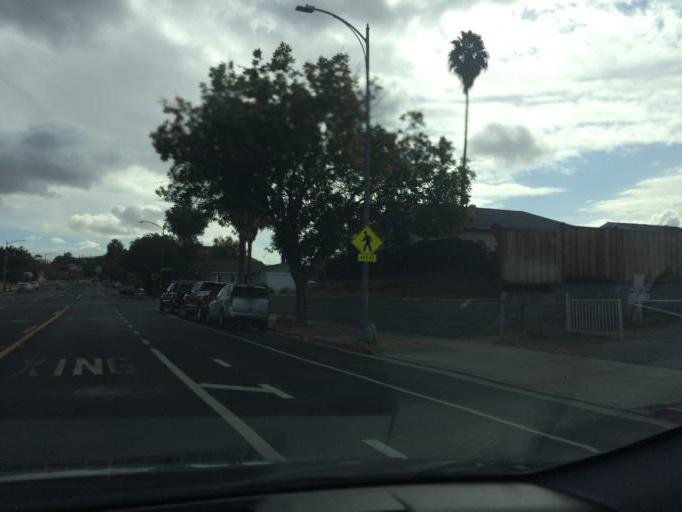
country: US
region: California
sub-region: Santa Clara County
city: Seven Trees
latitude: 37.3071
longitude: -121.7983
